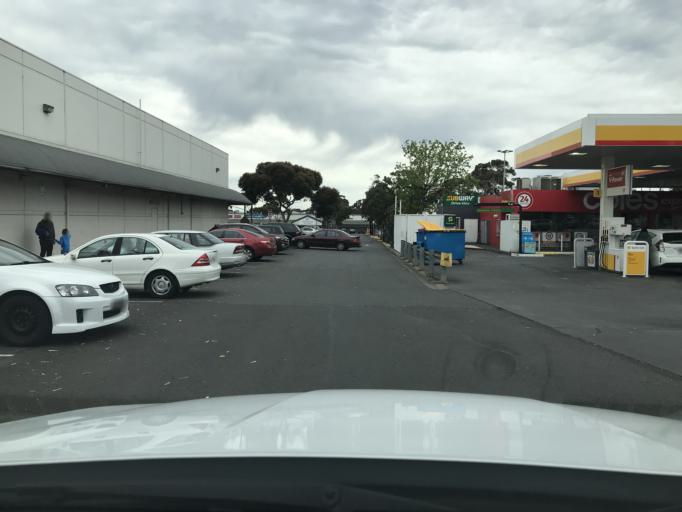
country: AU
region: Victoria
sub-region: Hume
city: Craigieburn
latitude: -37.5981
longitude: 144.9382
